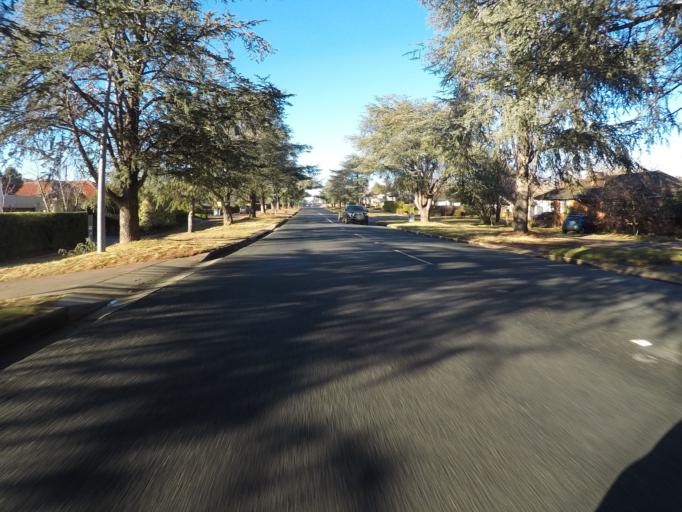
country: AU
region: Australian Capital Territory
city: Forrest
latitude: -35.3107
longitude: 149.0983
